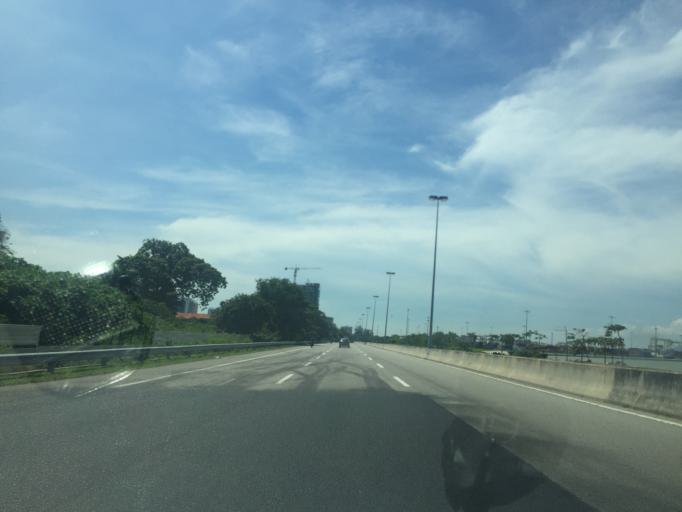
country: MY
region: Penang
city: Butterworth
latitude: 5.4240
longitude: 100.3745
